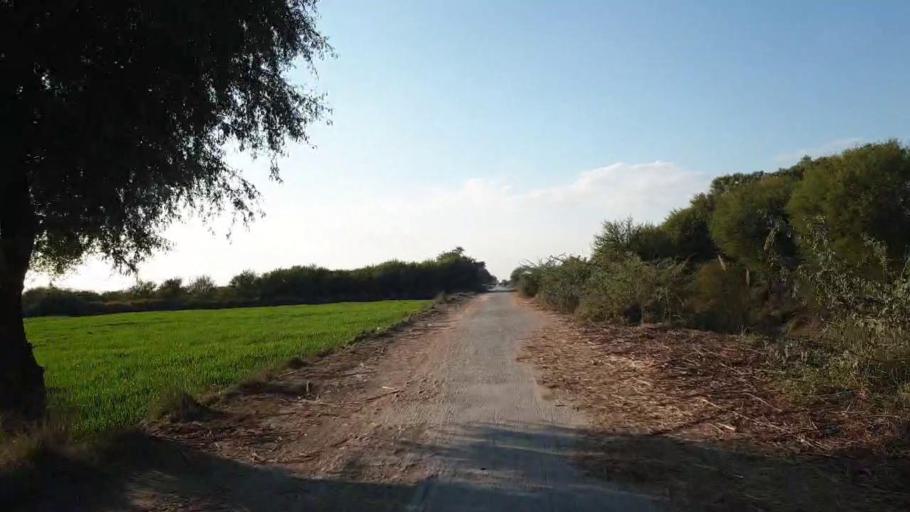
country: PK
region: Sindh
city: Shahpur Chakar
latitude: 26.1403
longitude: 68.5499
